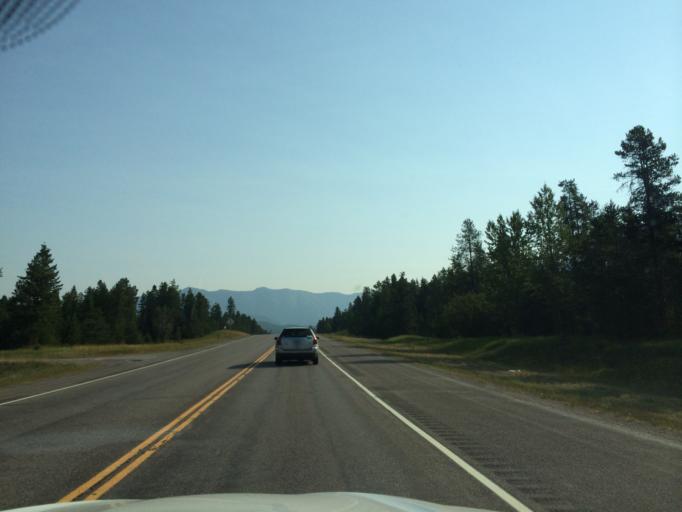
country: US
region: Montana
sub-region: Flathead County
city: Columbia Falls
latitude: 48.4547
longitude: -114.0136
